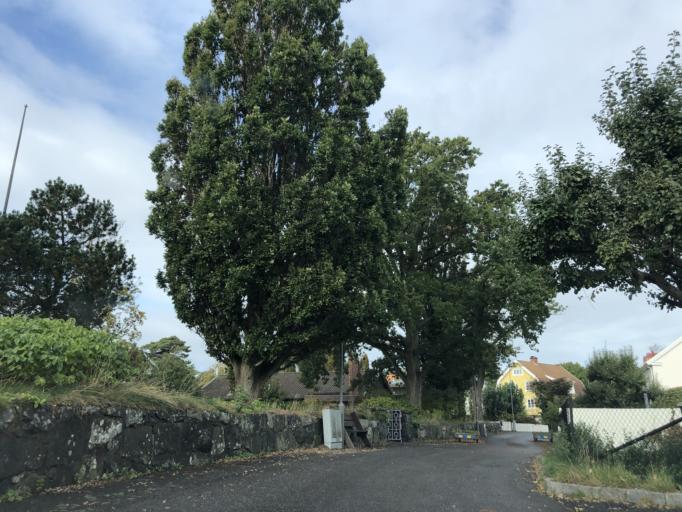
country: SE
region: Vaestra Goetaland
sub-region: Goteborg
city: Majorna
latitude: 57.6720
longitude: 11.8658
